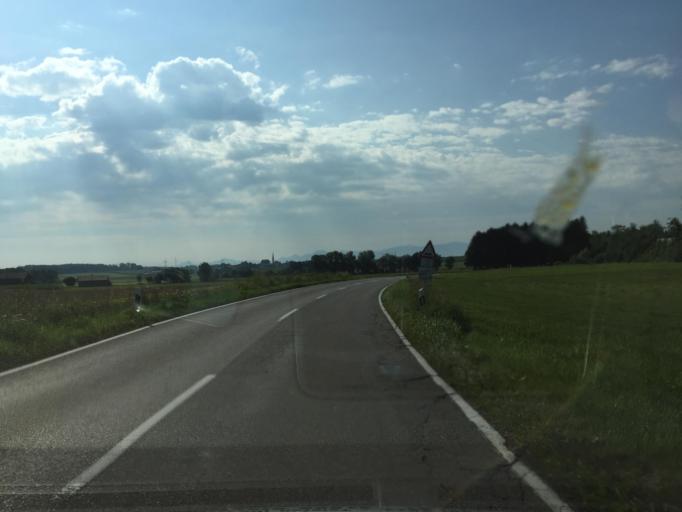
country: DE
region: Bavaria
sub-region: Upper Bavaria
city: Tuntenhausen
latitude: 47.9590
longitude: 12.0168
